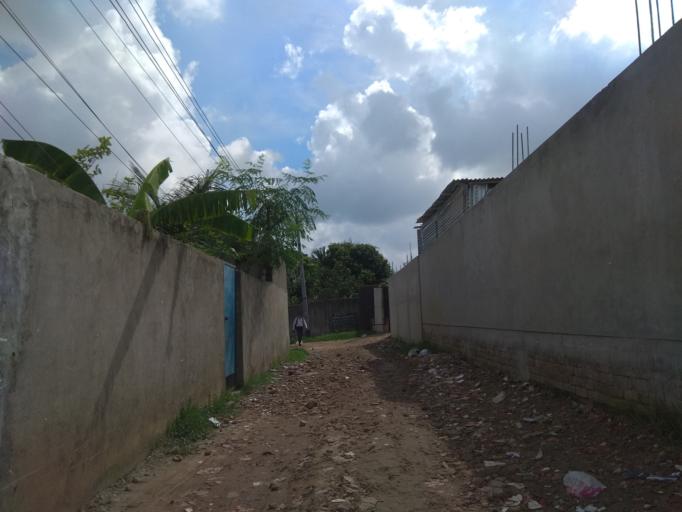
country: BD
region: Dhaka
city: Paltan
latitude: 23.8117
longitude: 90.3853
